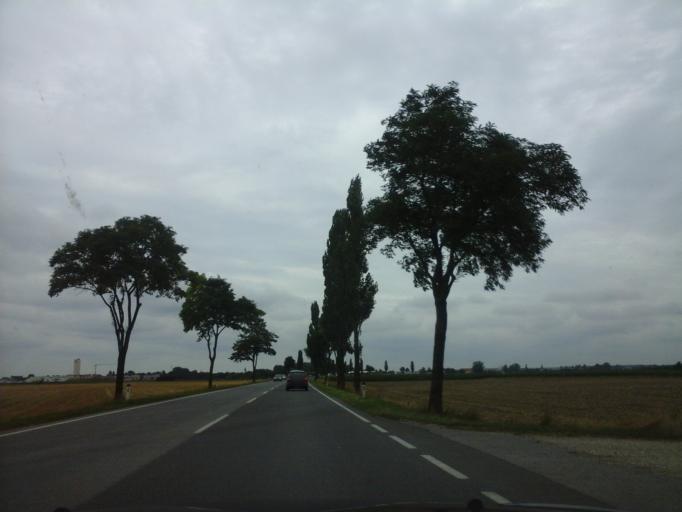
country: AT
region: Lower Austria
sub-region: Politischer Bezirk Ganserndorf
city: Engelhartstetten
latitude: 48.1680
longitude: 16.8938
